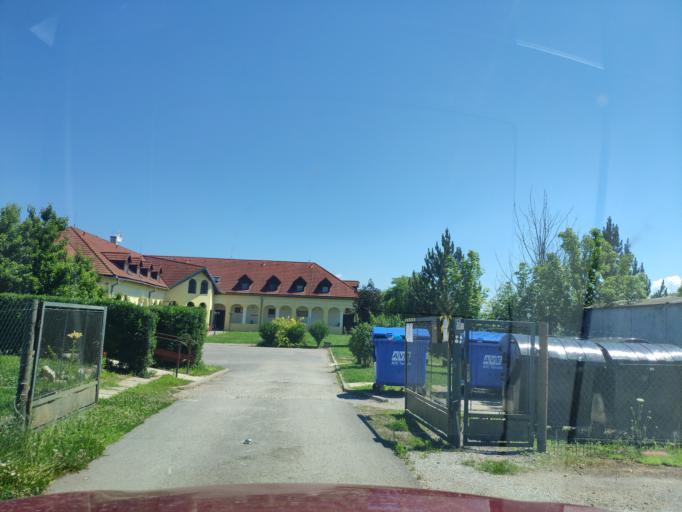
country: HU
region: Borsod-Abauj-Zemplen
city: Ozd
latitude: 48.3335
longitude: 20.2980
